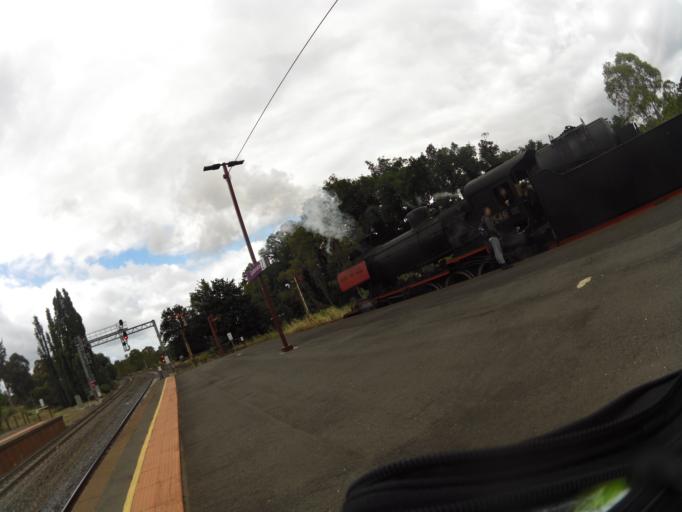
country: AU
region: Victoria
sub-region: Mount Alexander
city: Castlemaine
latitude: -37.0638
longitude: 144.2135
